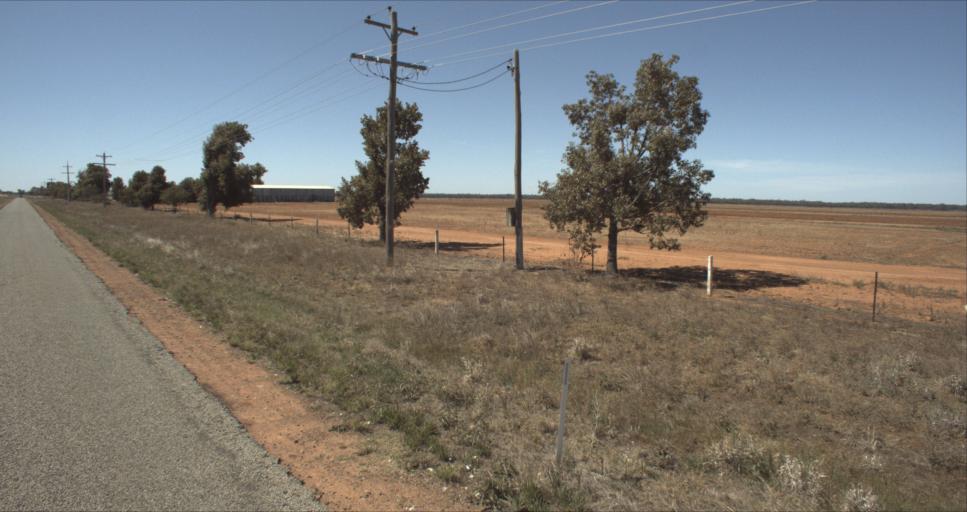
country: AU
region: New South Wales
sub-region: Leeton
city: Leeton
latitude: -34.5803
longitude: 146.2839
